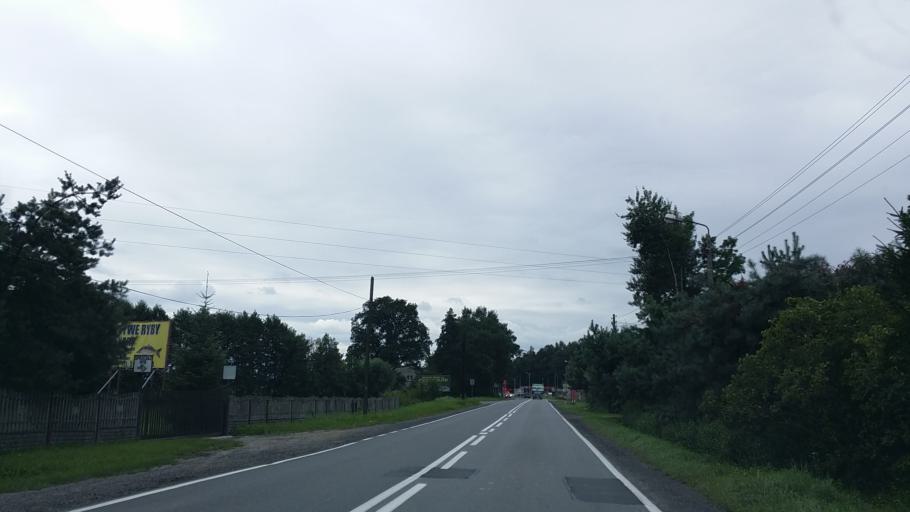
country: PL
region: Lesser Poland Voivodeship
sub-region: Powiat oswiecimski
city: Zator
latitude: 49.9865
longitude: 19.4379
